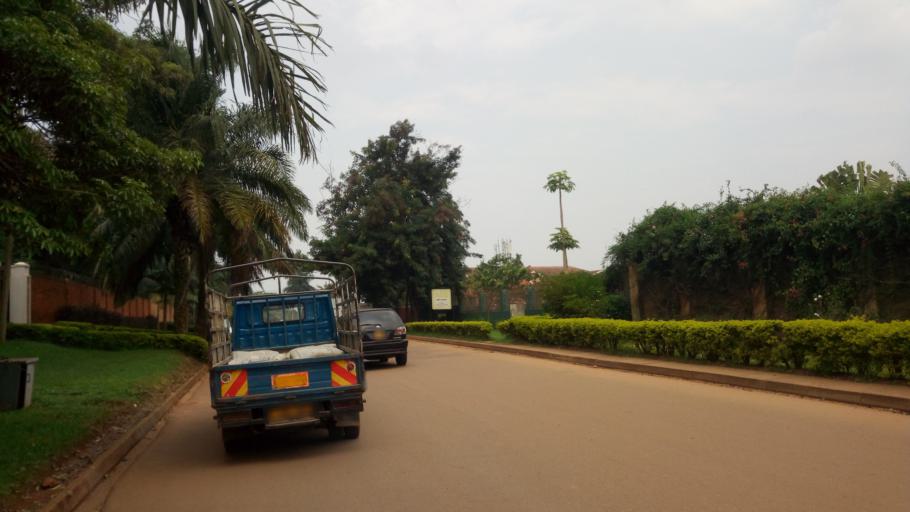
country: UG
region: Central Region
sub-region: Kampala District
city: Kampala
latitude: 0.3098
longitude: 32.6202
